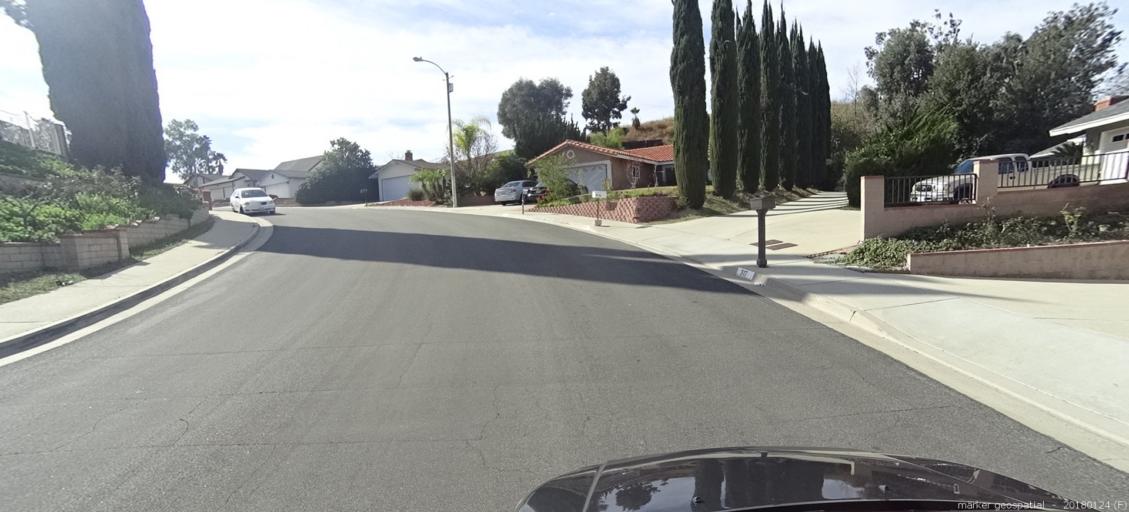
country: US
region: California
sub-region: Los Angeles County
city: Diamond Bar
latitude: 34.0255
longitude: -117.8193
